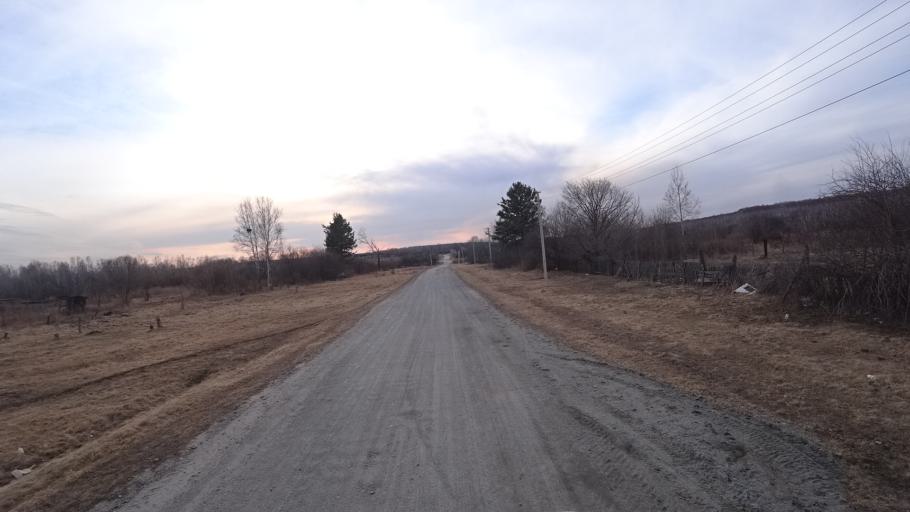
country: RU
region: Amur
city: Bureya
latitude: 50.0202
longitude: 129.7684
